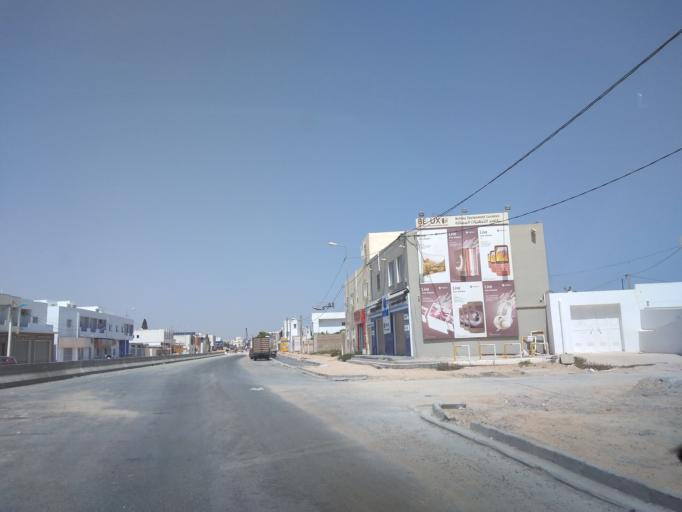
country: TN
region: Safaqis
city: Sfax
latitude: 34.7476
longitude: 10.7276
